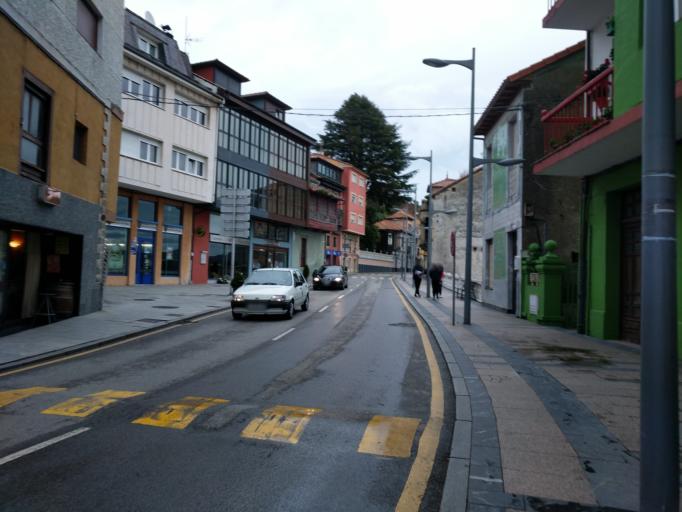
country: ES
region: Asturias
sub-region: Province of Asturias
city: Tineo
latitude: 43.3338
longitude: -6.4163
